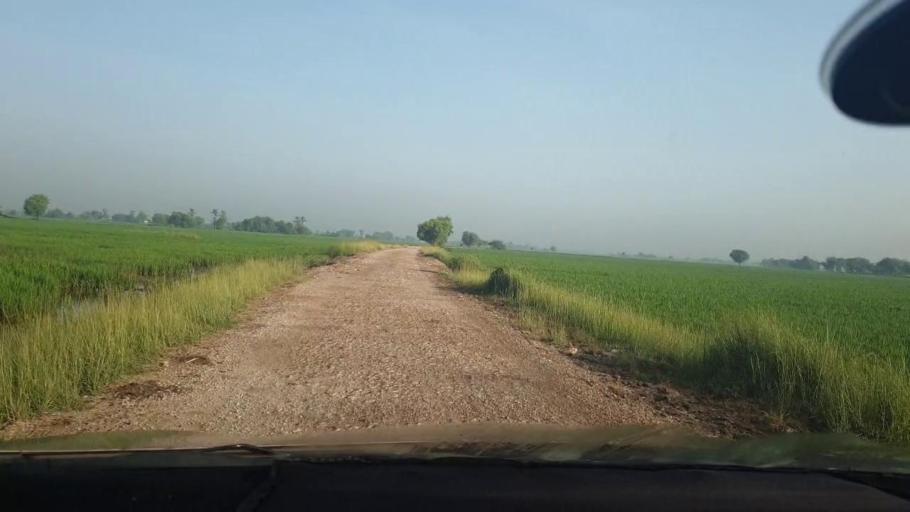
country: PK
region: Sindh
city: Kambar
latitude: 27.6176
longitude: 68.0197
